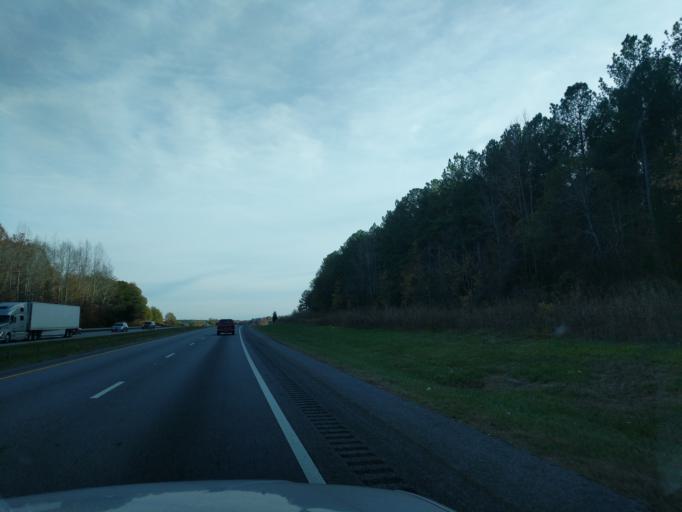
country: US
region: South Carolina
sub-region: Spartanburg County
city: Inman
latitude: 35.1197
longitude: -82.0901
